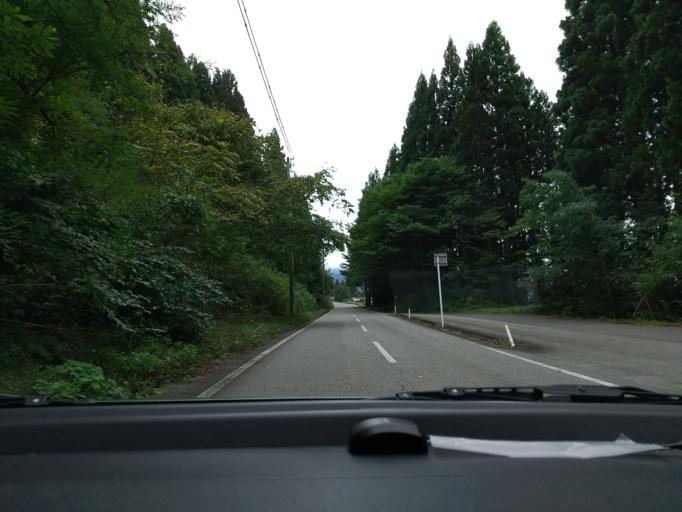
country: JP
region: Akita
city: Kakunodatemachi
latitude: 39.5440
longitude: 140.6374
